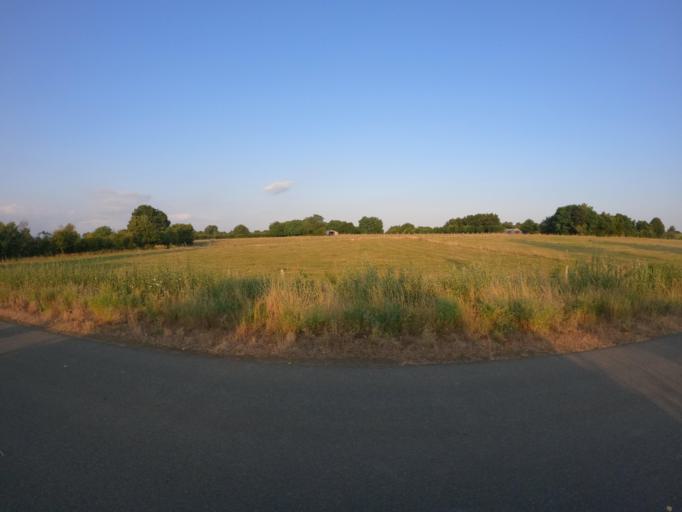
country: FR
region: Pays de la Loire
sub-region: Departement de la Sarthe
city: Brulon
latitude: 47.9128
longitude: -0.2288
